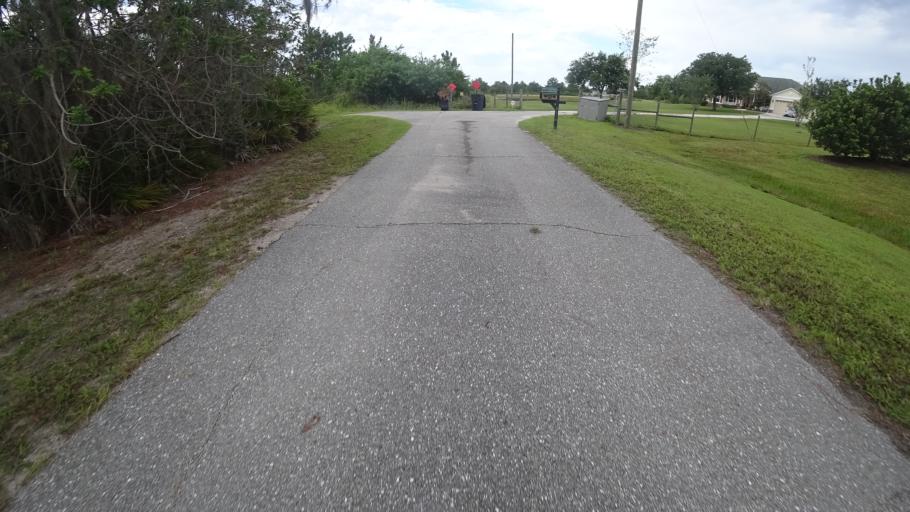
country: US
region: Florida
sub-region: Sarasota County
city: The Meadows
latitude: 27.4217
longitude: -82.2791
